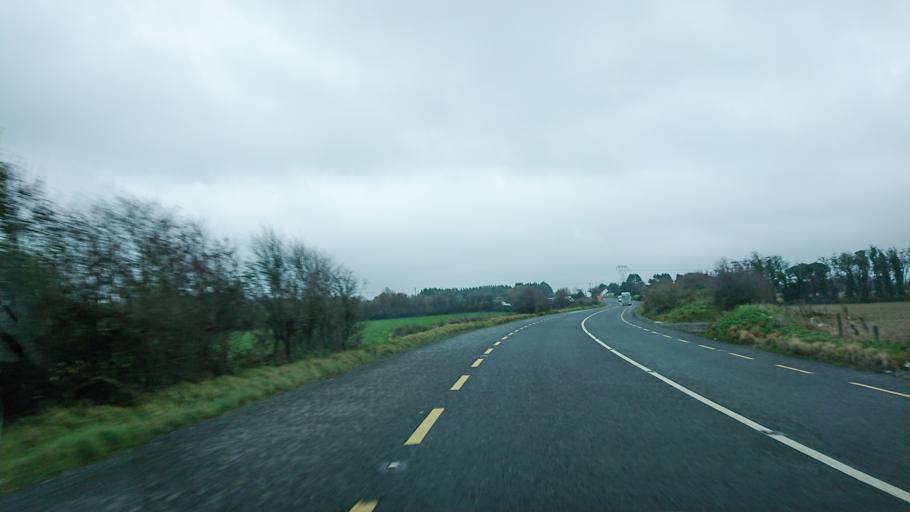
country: IE
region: Leinster
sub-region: Kilkenny
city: Mooncoin
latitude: 52.2828
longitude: -7.1951
